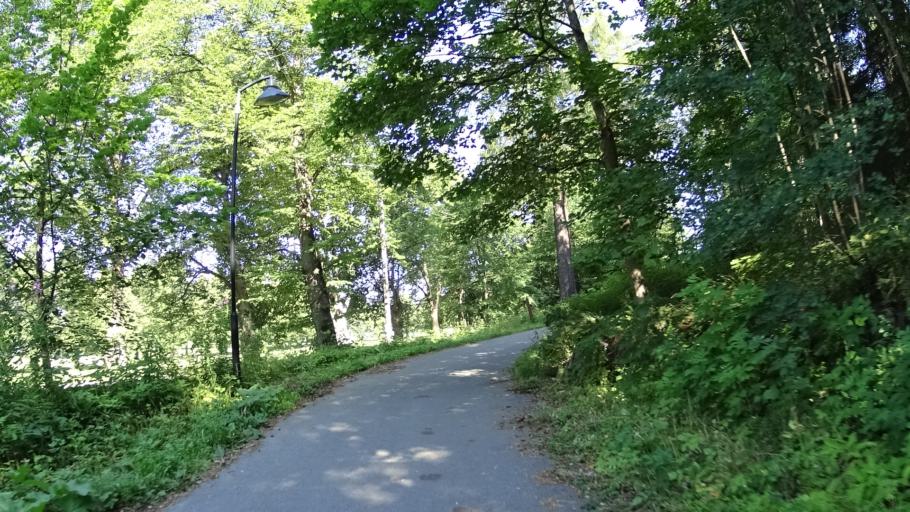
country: FI
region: Haeme
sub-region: Haemeenlinna
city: Haemeenlinna
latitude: 61.0247
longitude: 24.4457
